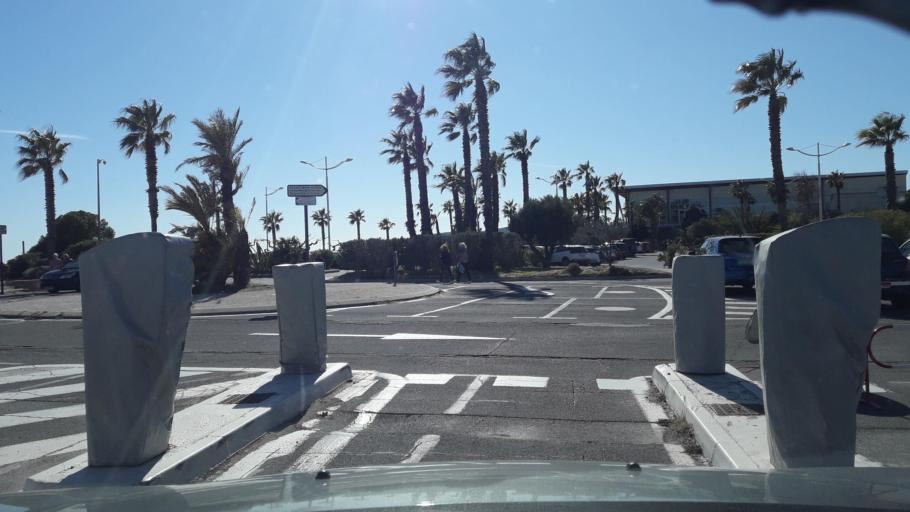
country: FR
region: Provence-Alpes-Cote d'Azur
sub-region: Departement du Var
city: Frejus
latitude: 43.4179
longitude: 6.7444
